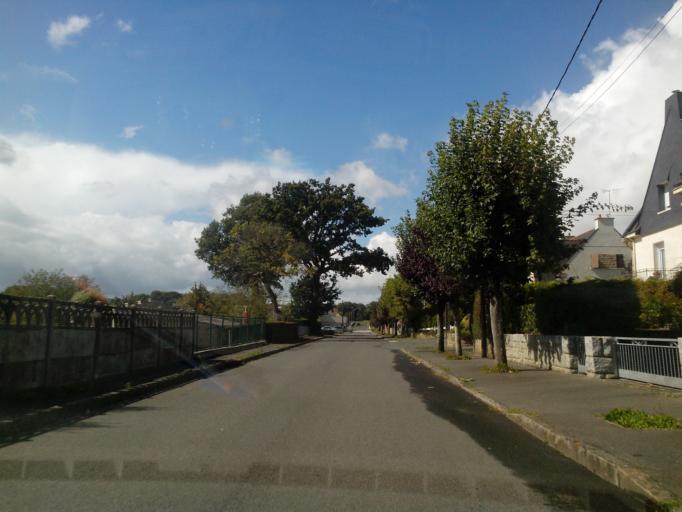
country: FR
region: Brittany
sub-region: Departement des Cotes-d'Armor
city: Merdrignac
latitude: 48.1921
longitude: -2.4183
